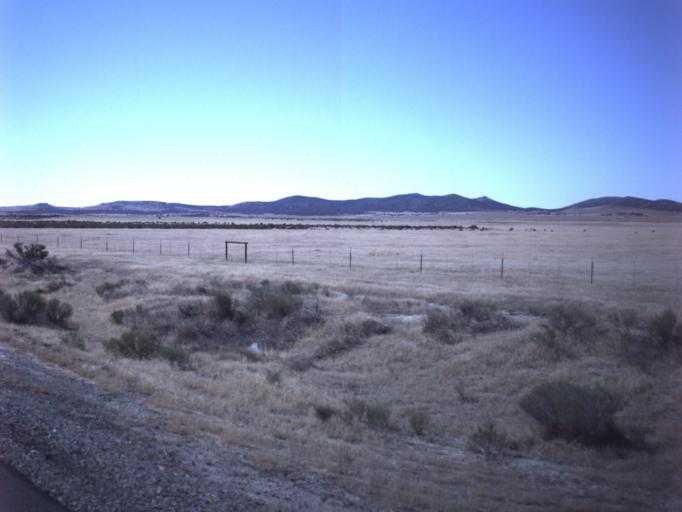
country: US
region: Utah
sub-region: Tooele County
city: Grantsville
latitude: 40.3007
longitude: -112.7428
